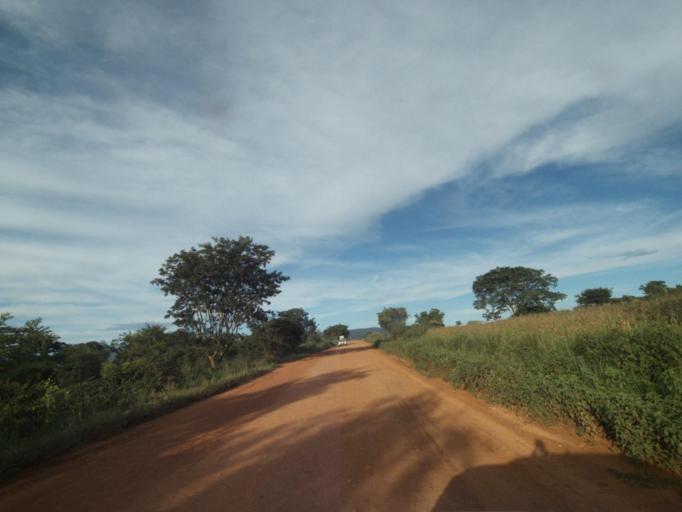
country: BR
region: Goias
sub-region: Jaragua
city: Jaragua
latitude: -15.8522
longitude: -49.3782
